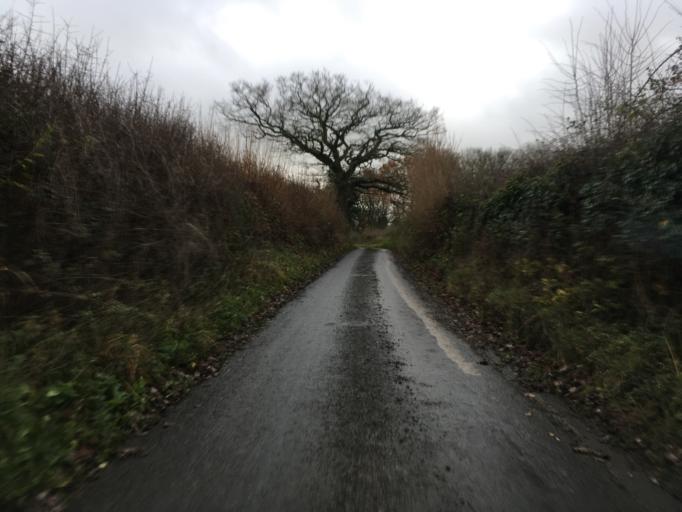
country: GB
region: England
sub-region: Wiltshire
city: Nettleton
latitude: 51.5135
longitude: -2.2720
